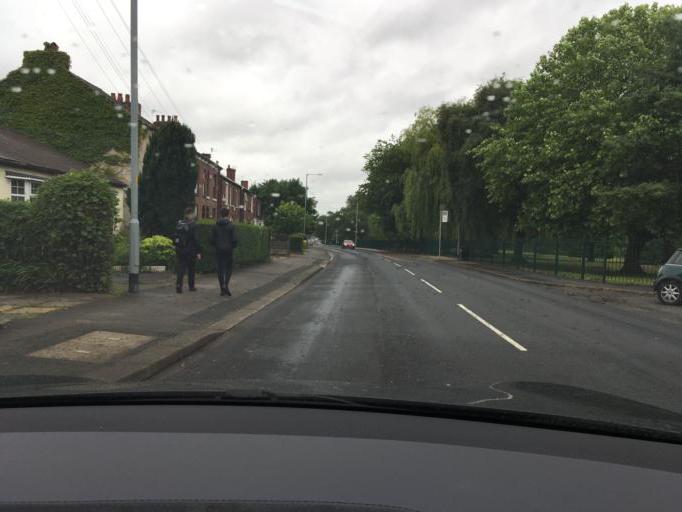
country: GB
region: England
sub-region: Borough of Stockport
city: Cheadle Hulme
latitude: 53.3873
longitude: -2.1825
